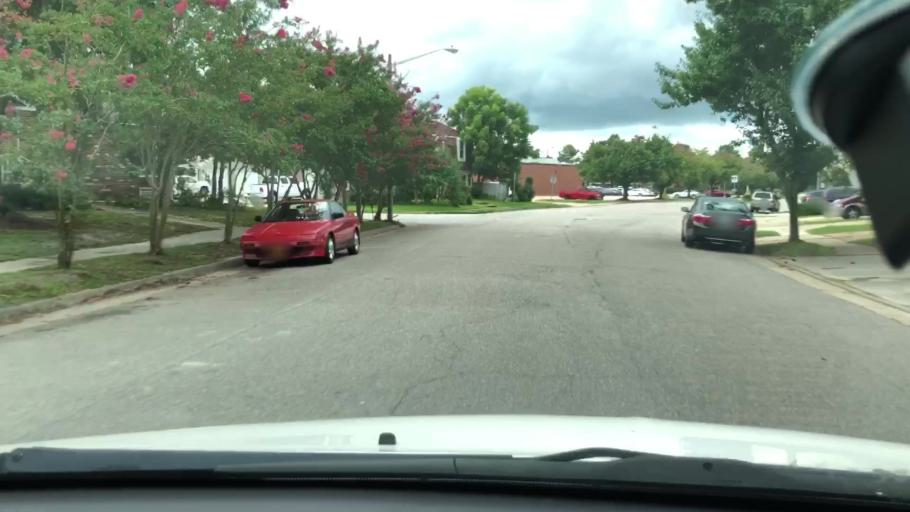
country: US
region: Virginia
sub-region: City of Virginia Beach
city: Virginia Beach
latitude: 36.8446
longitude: -76.1148
